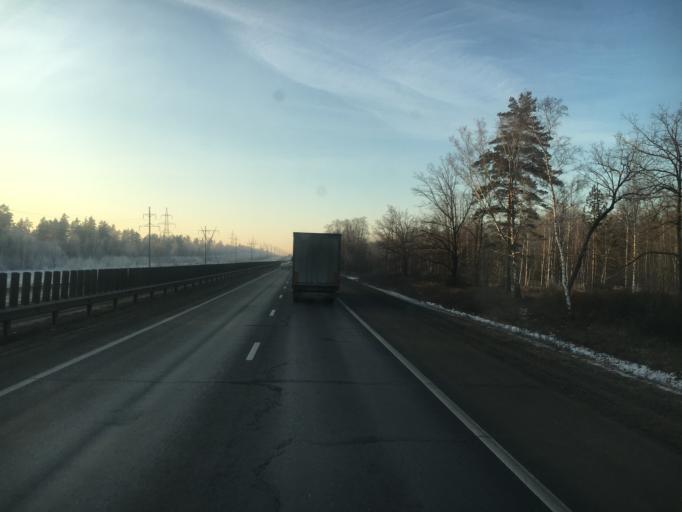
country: RU
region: Samara
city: Pribrezhnyy
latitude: 53.5148
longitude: 49.8865
